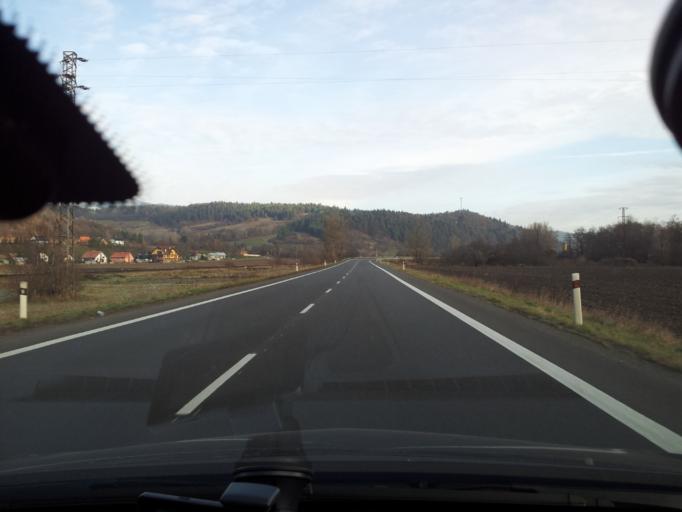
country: SK
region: Banskobystricky
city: Hrochot,Slovakia
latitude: 48.7665
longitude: 19.2837
